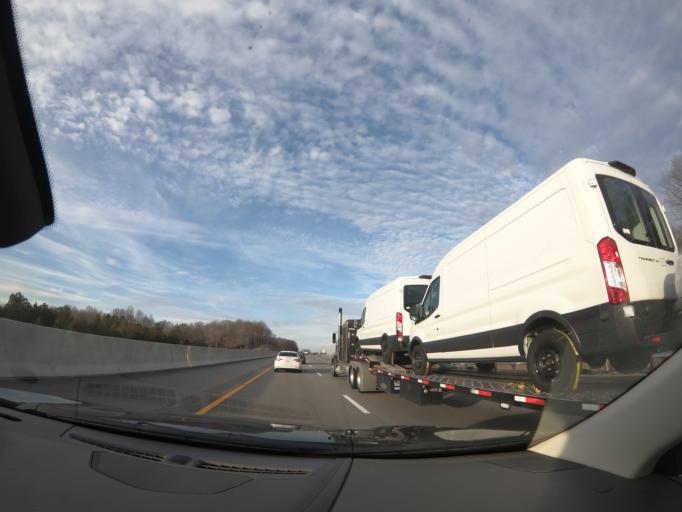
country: US
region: Kentucky
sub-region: Hart County
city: Munfordville
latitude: 37.3392
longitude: -85.9067
